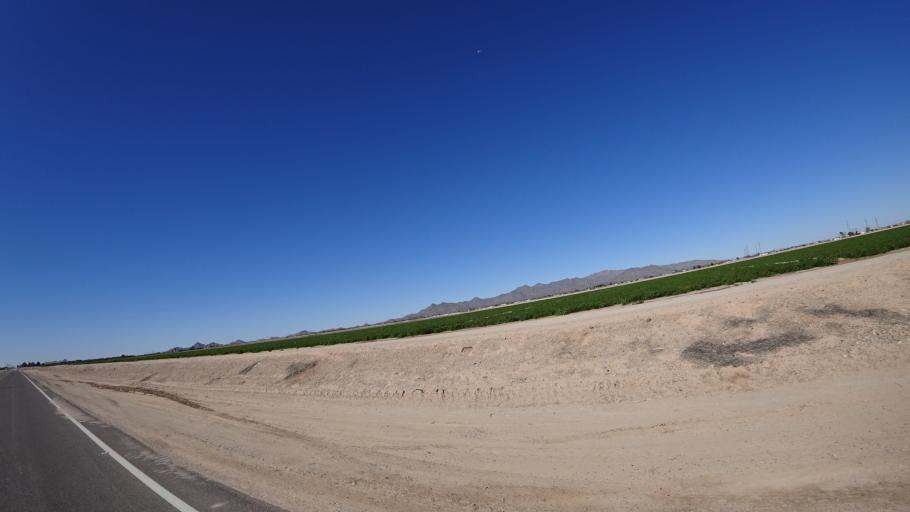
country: US
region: Arizona
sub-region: Maricopa County
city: Buckeye
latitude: 33.4068
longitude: -112.5279
